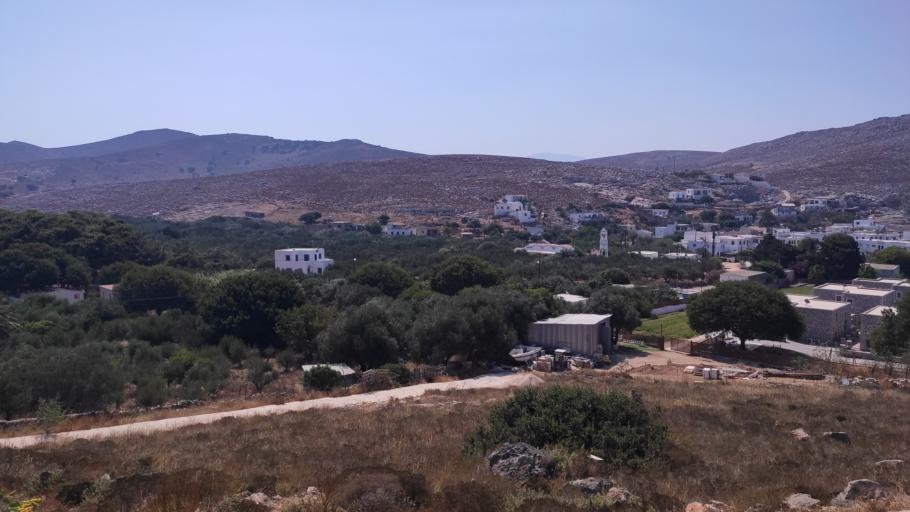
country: GR
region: South Aegean
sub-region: Nomos Dodekanisou
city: Pylion
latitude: 36.9350
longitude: 27.1338
